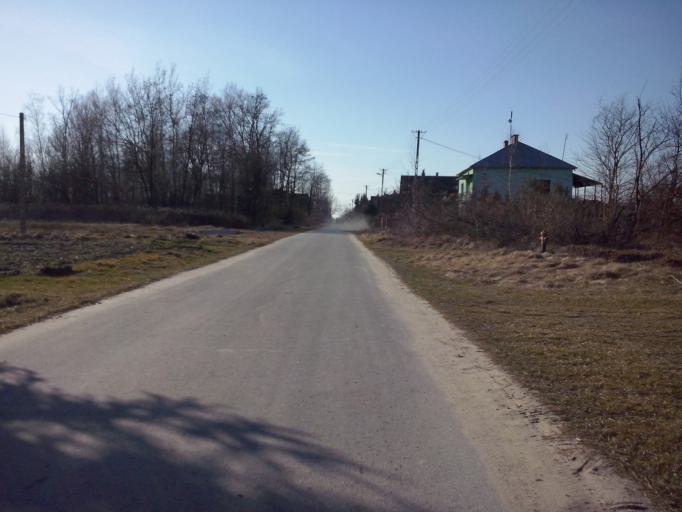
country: PL
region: Subcarpathian Voivodeship
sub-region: Powiat nizanski
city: Krzeszow
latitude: 50.4141
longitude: 22.3799
